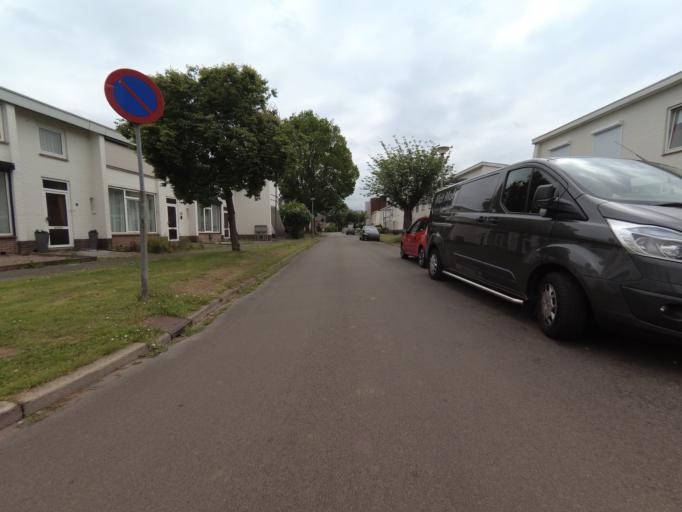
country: NL
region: Limburg
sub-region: Gemeente Maastricht
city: Heer
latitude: 50.8631
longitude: 5.7293
